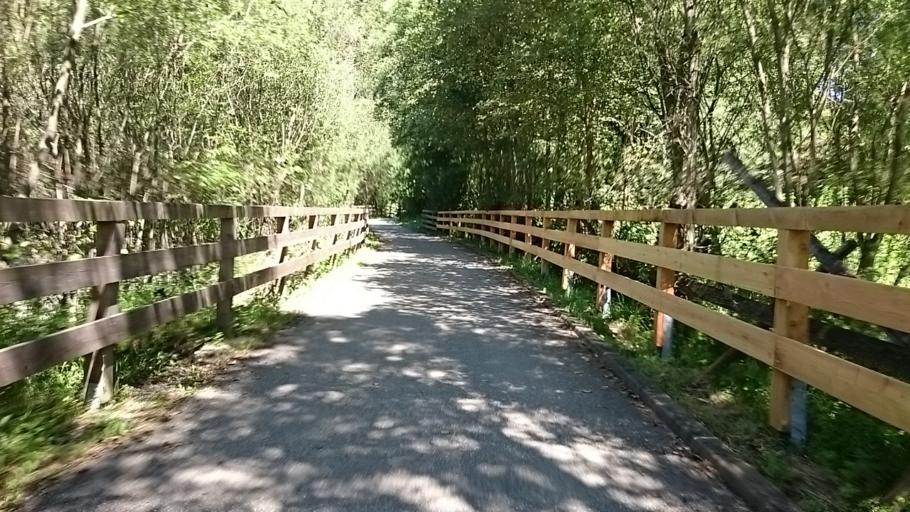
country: IT
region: Trentino-Alto Adige
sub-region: Bolzano
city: San Lorenzo di Sebato
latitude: 46.7778
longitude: 11.8848
